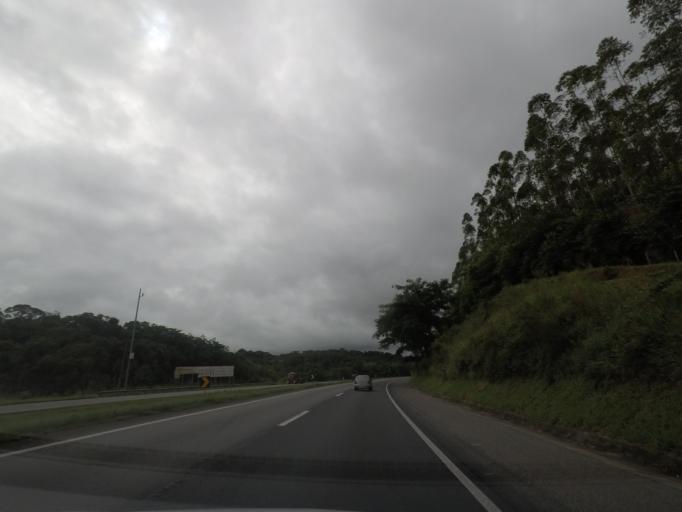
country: BR
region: Sao Paulo
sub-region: Registro
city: Registro
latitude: -24.5692
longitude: -47.8787
